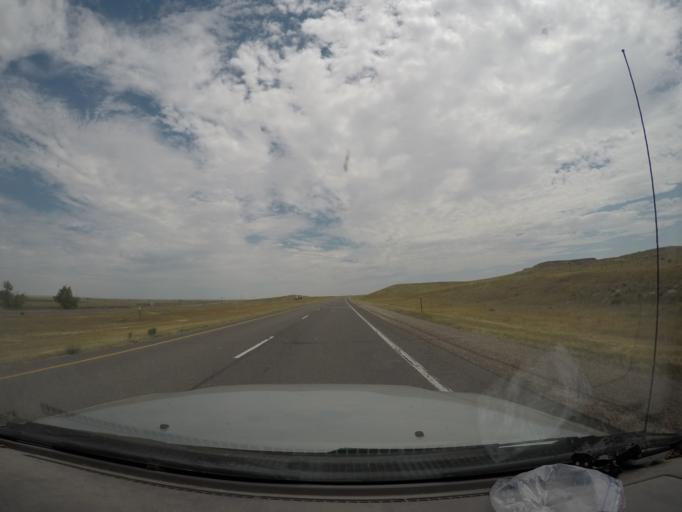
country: US
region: Wyoming
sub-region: Laramie County
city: Pine Bluffs
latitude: 41.1914
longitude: -103.9969
